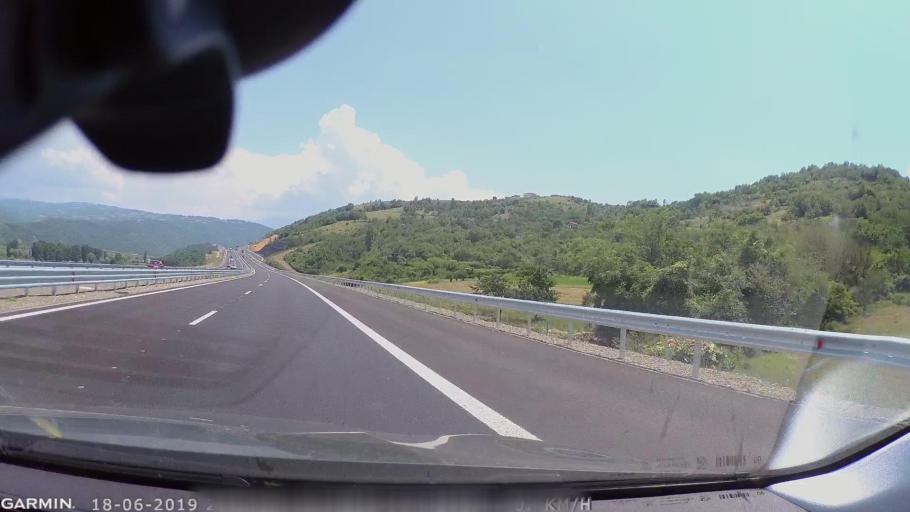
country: BG
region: Blagoevgrad
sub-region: Obshtina Blagoevgrad
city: Blagoevgrad
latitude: 41.9787
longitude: 23.0663
